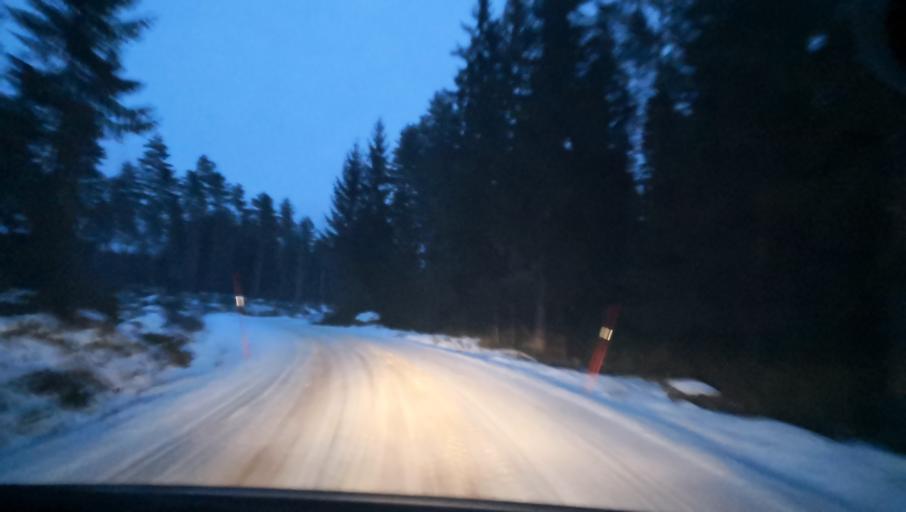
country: SE
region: Dalarna
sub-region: Avesta Kommun
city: Horndal
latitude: 60.2404
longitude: 16.6736
